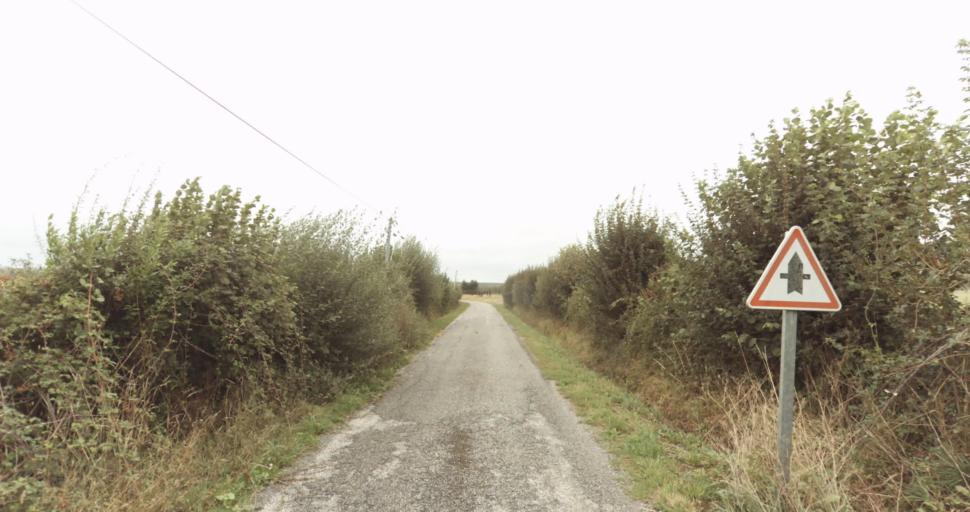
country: FR
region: Lower Normandy
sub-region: Departement de l'Orne
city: Sainte-Gauburge-Sainte-Colombe
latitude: 48.7185
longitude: 0.4606
